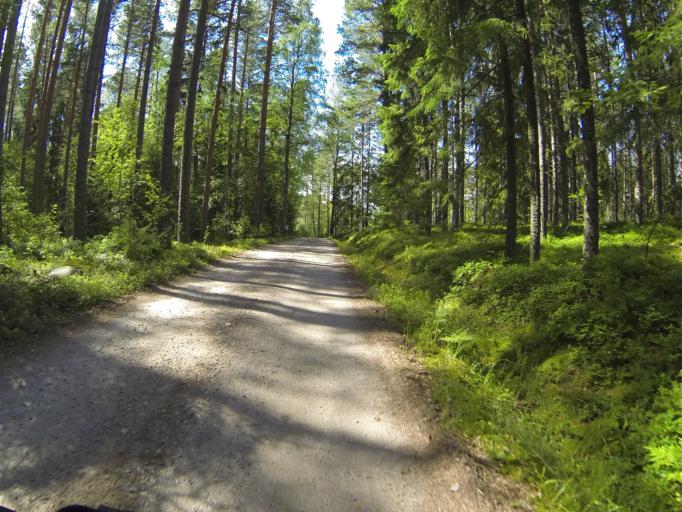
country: FI
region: Varsinais-Suomi
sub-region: Salo
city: Pernioe
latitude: 60.2796
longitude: 23.0284
